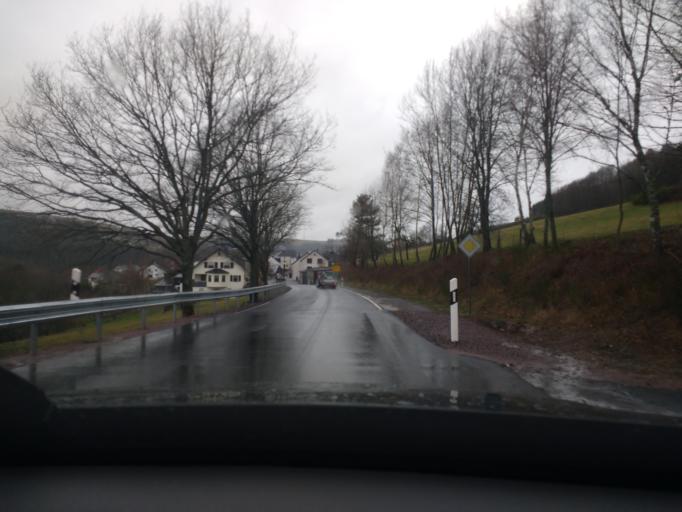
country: DE
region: Rheinland-Pfalz
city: Hinzenburg
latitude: 49.6622
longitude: 6.7291
